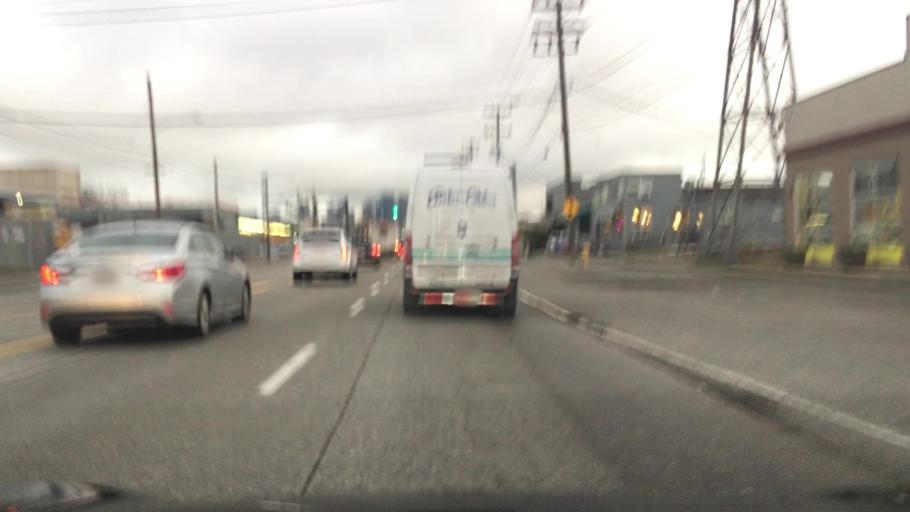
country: US
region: Washington
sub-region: King County
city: Seattle
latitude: 47.5685
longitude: -122.3290
